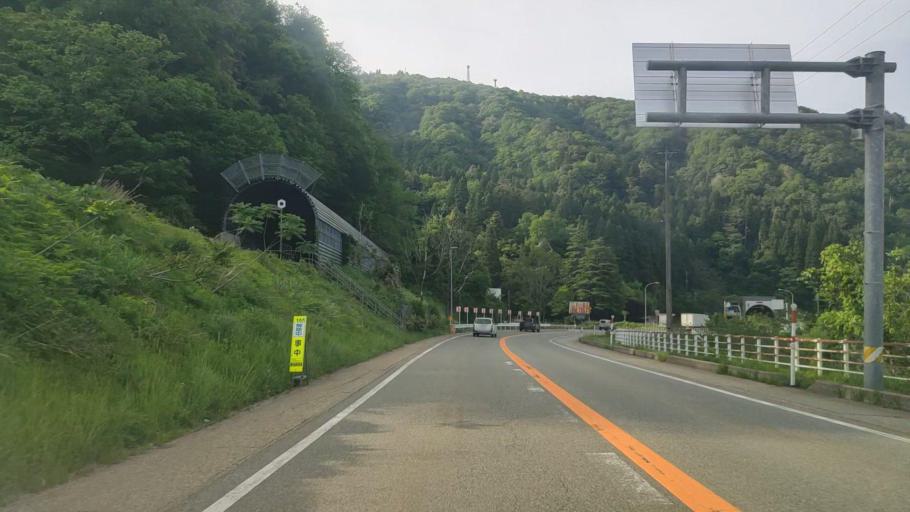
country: JP
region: Toyama
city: Yatsuomachi-higashikumisaka
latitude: 36.4939
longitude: 137.2359
